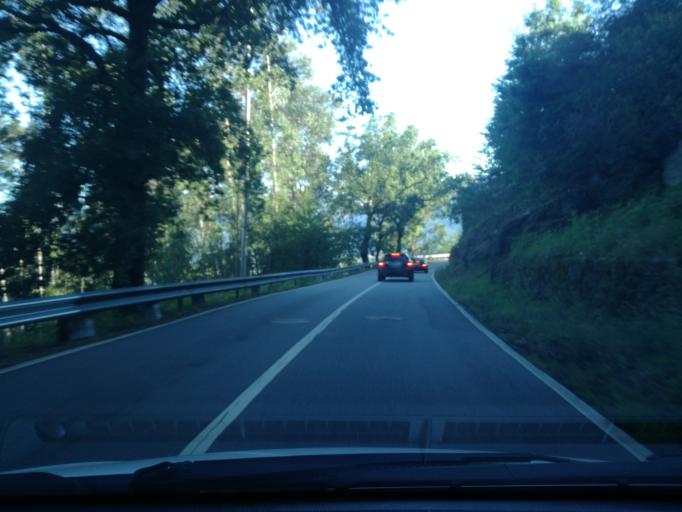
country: PT
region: Braga
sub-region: Vieira do Minho
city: Real
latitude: 41.6476
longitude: -8.1854
